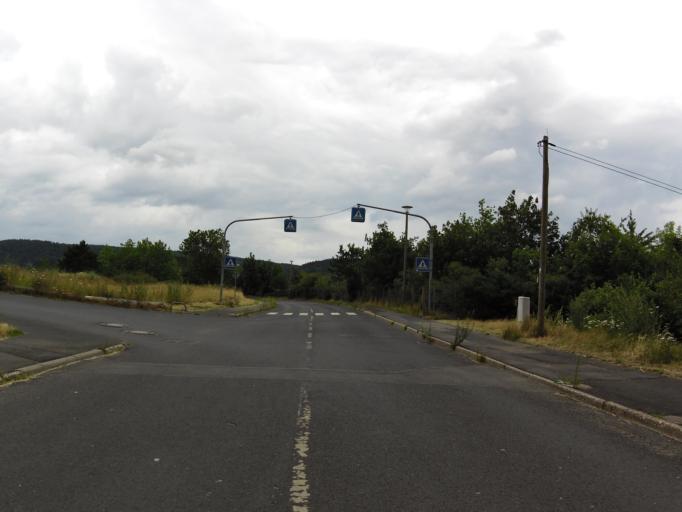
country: DE
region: Thuringia
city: Bad Salzungen
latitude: 50.8090
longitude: 10.2540
